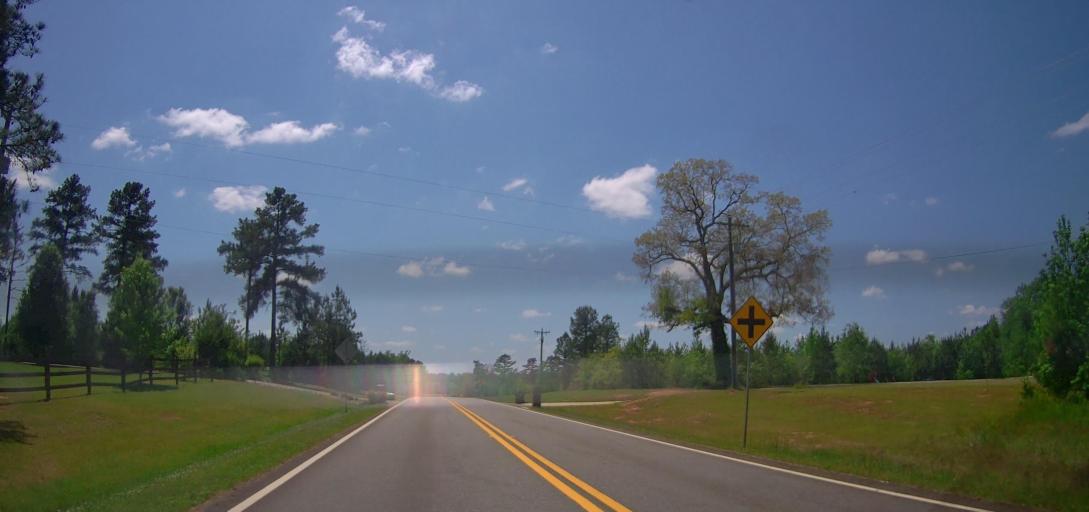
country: US
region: Georgia
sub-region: Jasper County
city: Monticello
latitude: 33.2947
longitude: -83.6415
